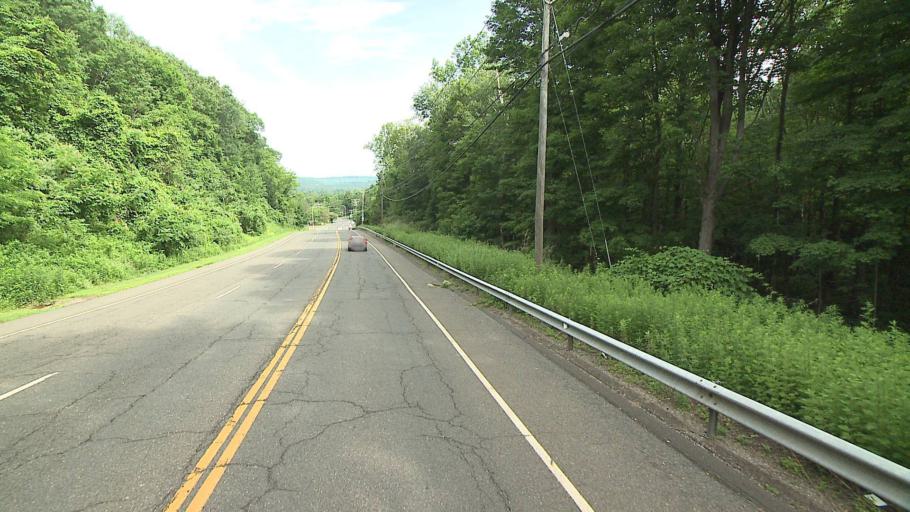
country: US
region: Connecticut
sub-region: New Haven County
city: Southbury
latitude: 41.4734
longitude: -73.2077
